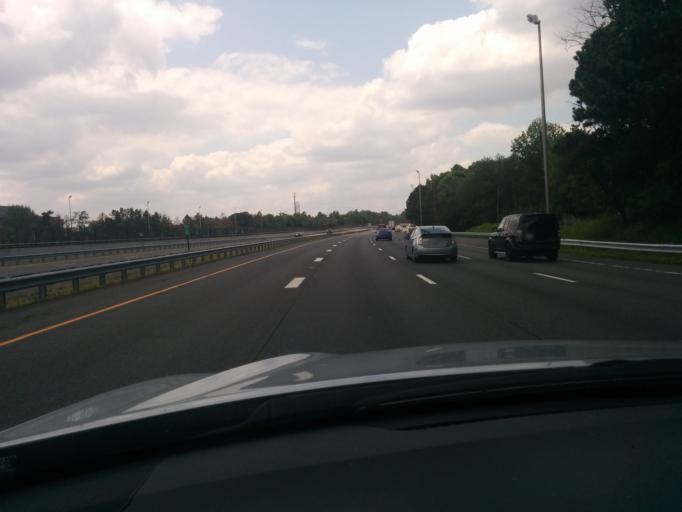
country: US
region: Virginia
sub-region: Fairfax County
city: Reston
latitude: 38.9462
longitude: -77.3190
